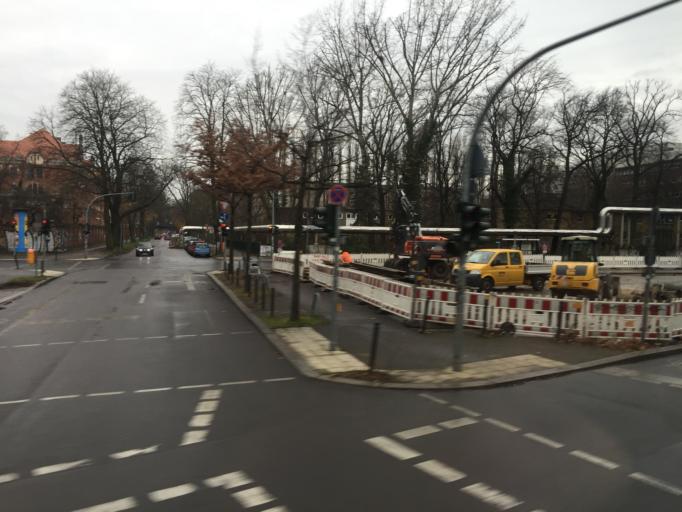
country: DE
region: Berlin
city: Treptow Bezirk
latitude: 52.4943
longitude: 13.4550
